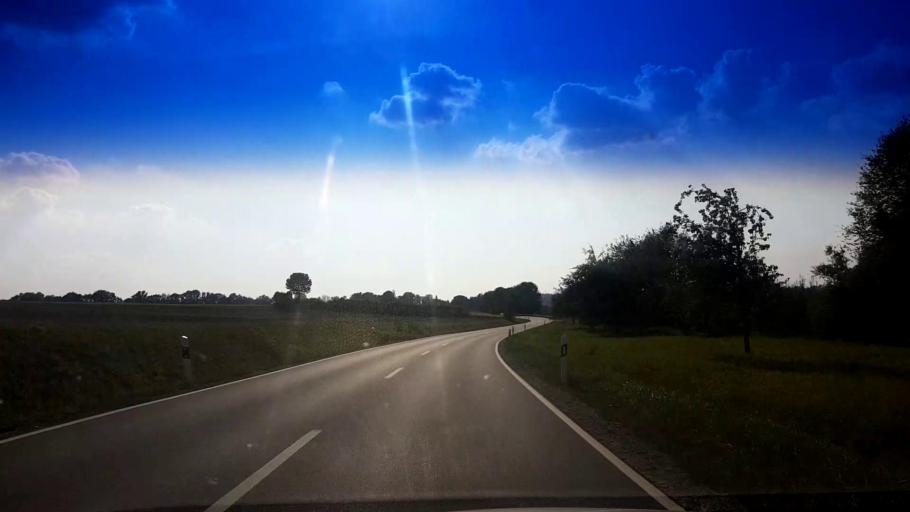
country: DE
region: Bavaria
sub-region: Upper Franconia
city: Schesslitz
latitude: 49.9622
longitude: 11.0105
